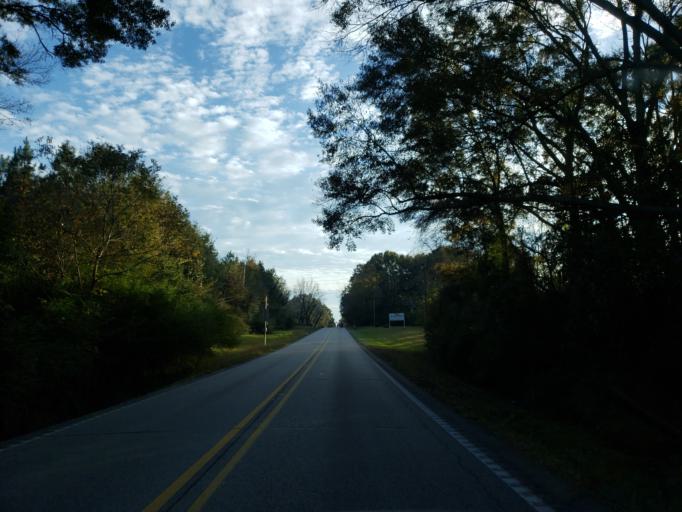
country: US
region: Mississippi
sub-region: Lamar County
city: Purvis
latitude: 31.1303
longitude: -89.4065
